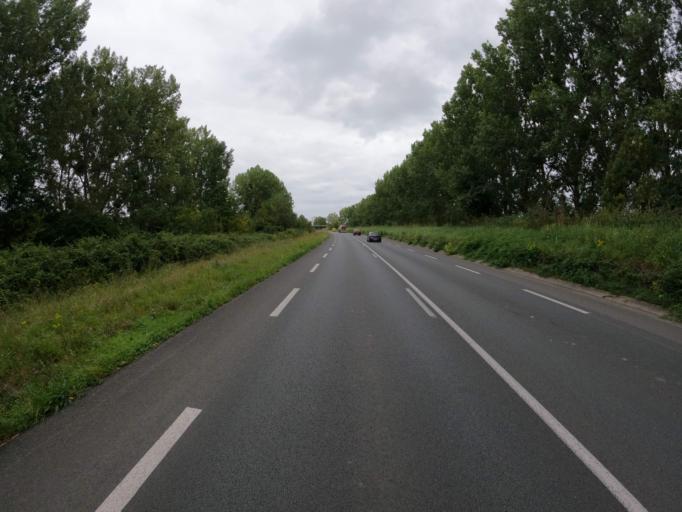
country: FR
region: Pays de la Loire
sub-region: Departement de la Vendee
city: Fontenay-le-Comte
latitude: 46.4574
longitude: -0.8365
